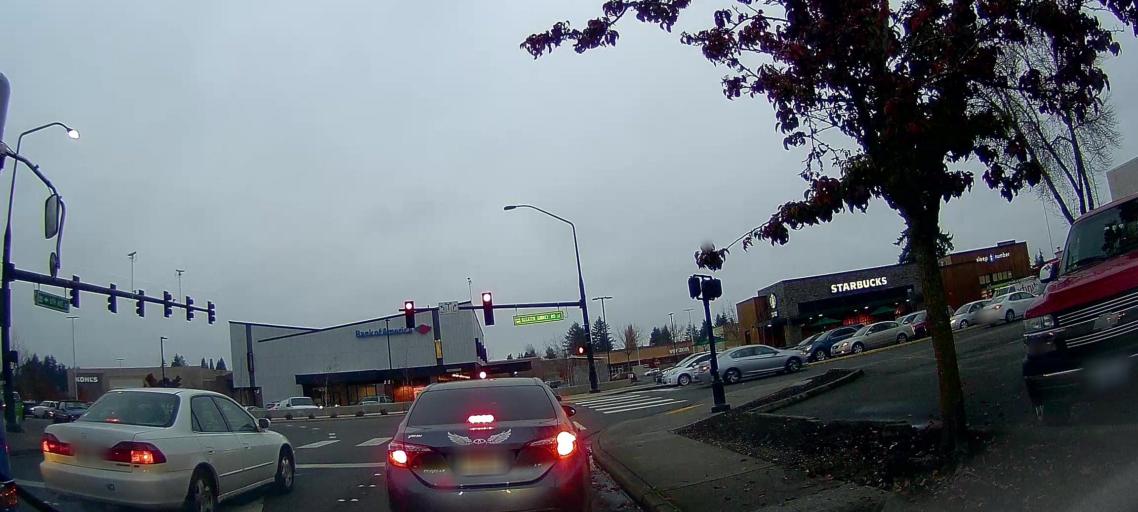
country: US
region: Washington
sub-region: Thurston County
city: Lacey
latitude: 47.0432
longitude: -122.8334
